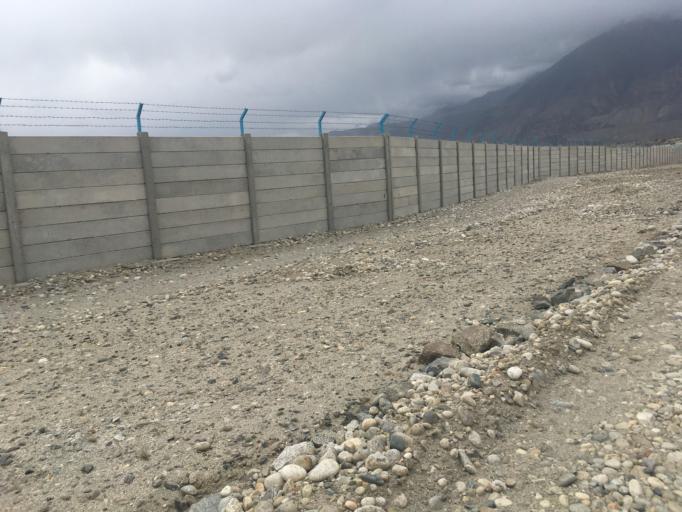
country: PK
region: Gilgit-Baltistan
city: Skardu
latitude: 35.3125
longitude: 75.6579
